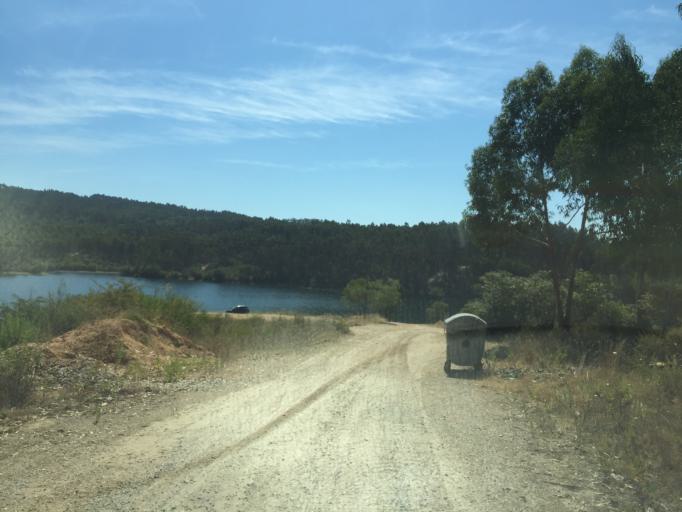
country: PT
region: Santarem
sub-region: Tomar
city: Tomar
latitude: 39.6166
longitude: -8.3612
